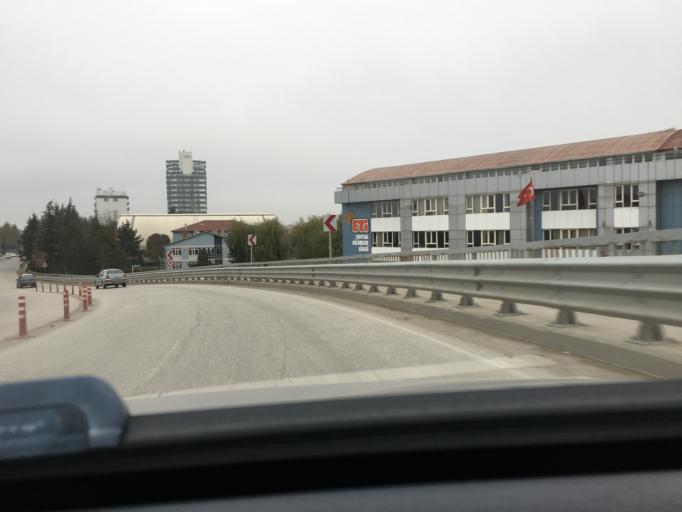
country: TR
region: Eskisehir
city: Eskisehir
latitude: 39.7686
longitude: 30.4823
